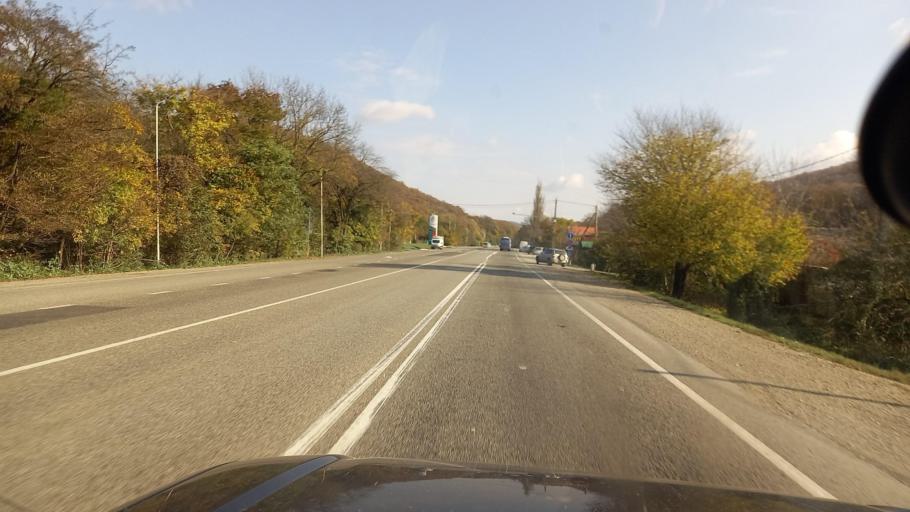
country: RU
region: Krasnodarskiy
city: Verkhnebakanskiy
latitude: 44.8490
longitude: 37.7222
